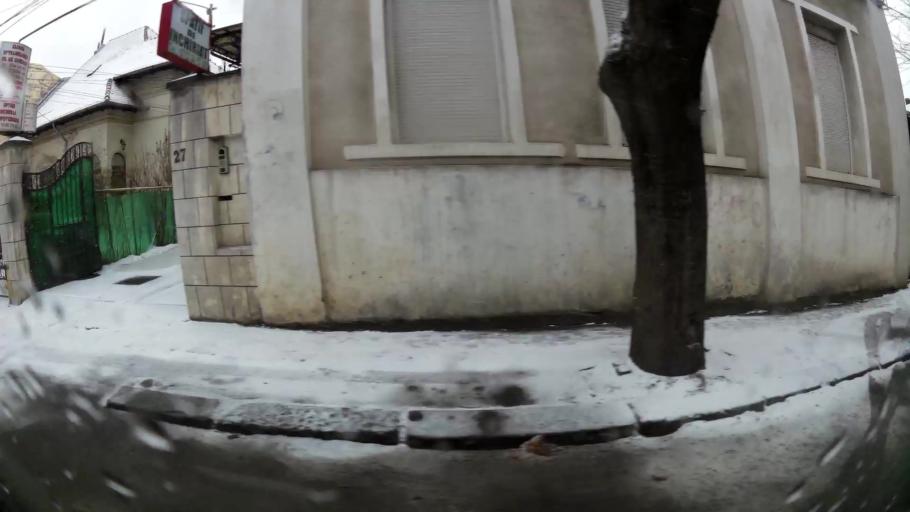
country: RO
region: Prahova
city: Ploiesti
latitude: 44.9386
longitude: 26.0191
